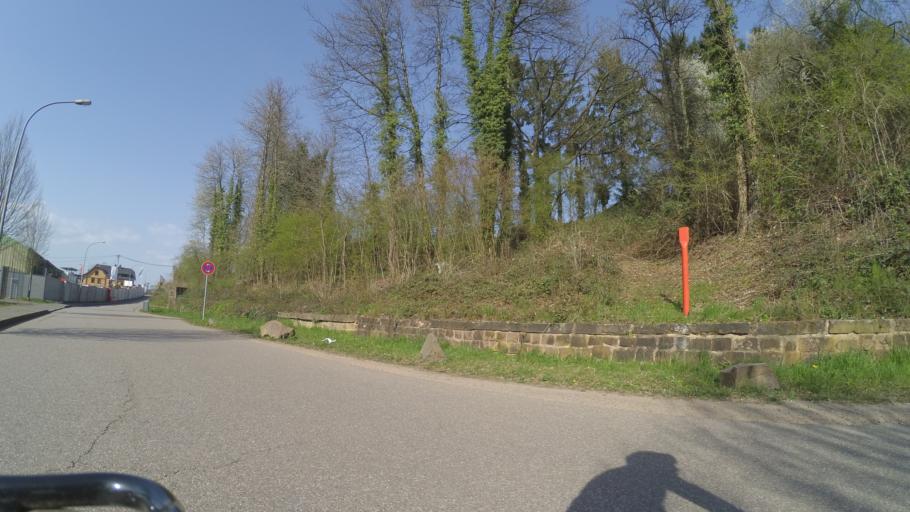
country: DE
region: Saarland
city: Heusweiler
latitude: 49.3292
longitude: 6.9414
